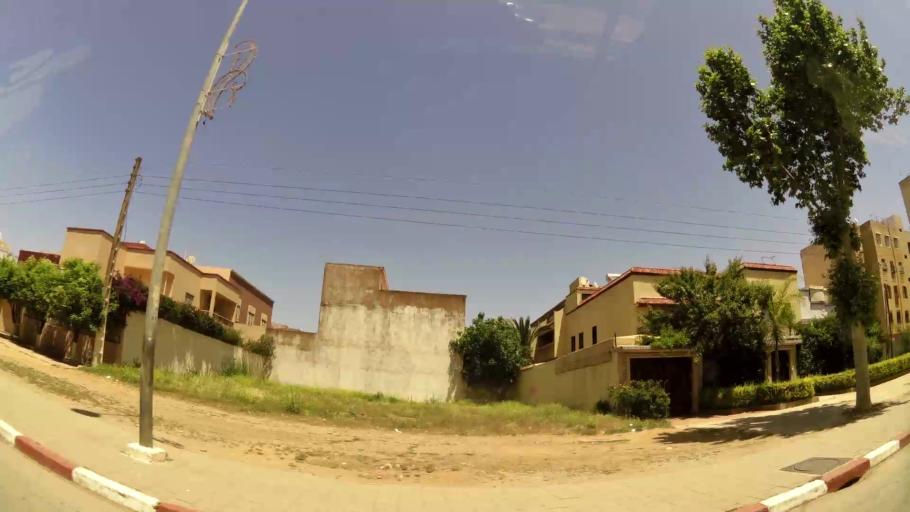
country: MA
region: Rabat-Sale-Zemmour-Zaer
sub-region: Khemisset
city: Khemisset
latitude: 33.8270
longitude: -6.0859
